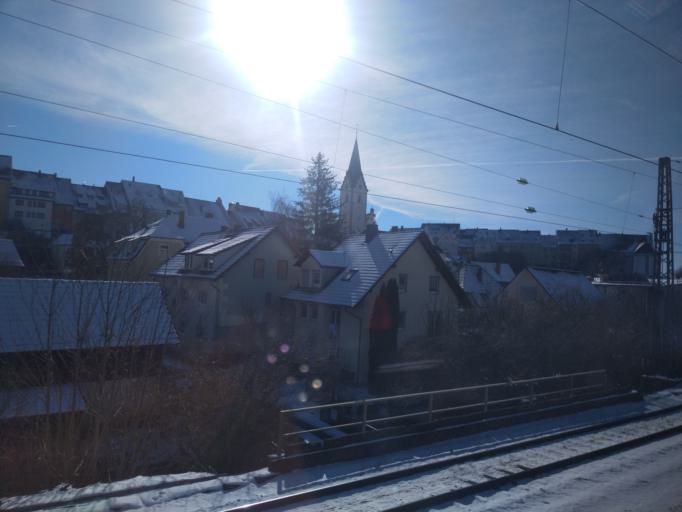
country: DE
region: Baden-Wuerttemberg
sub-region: Freiburg Region
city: Engen
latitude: 47.8550
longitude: 8.7708
